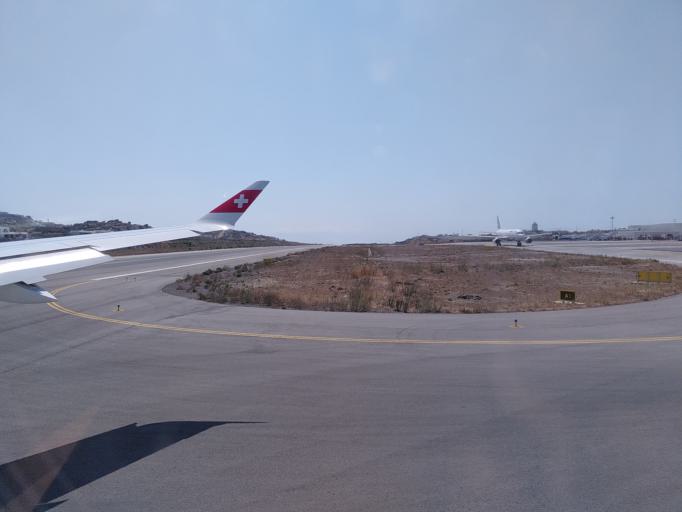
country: GR
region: South Aegean
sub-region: Nomos Kykladon
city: Mykonos
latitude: 37.4366
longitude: 25.3473
